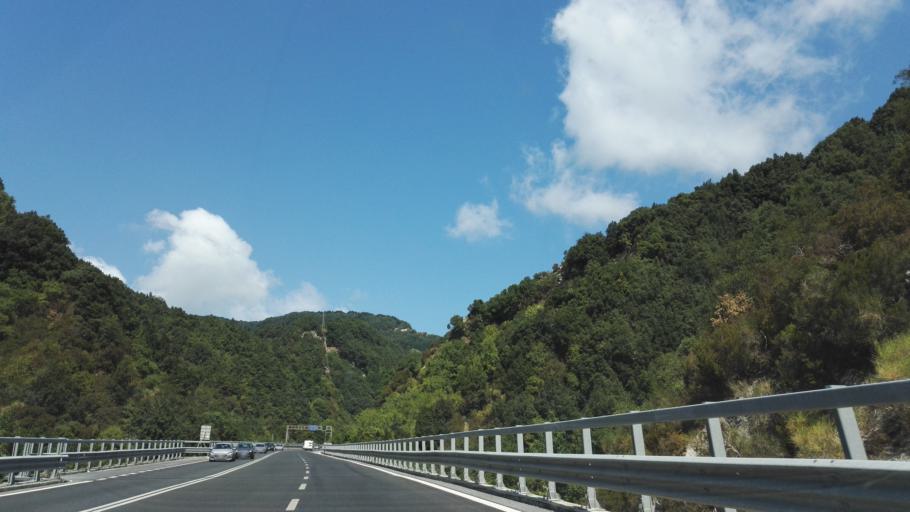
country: IT
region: Calabria
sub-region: Provincia di Reggio Calabria
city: Amato
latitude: 38.3720
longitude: 16.1809
